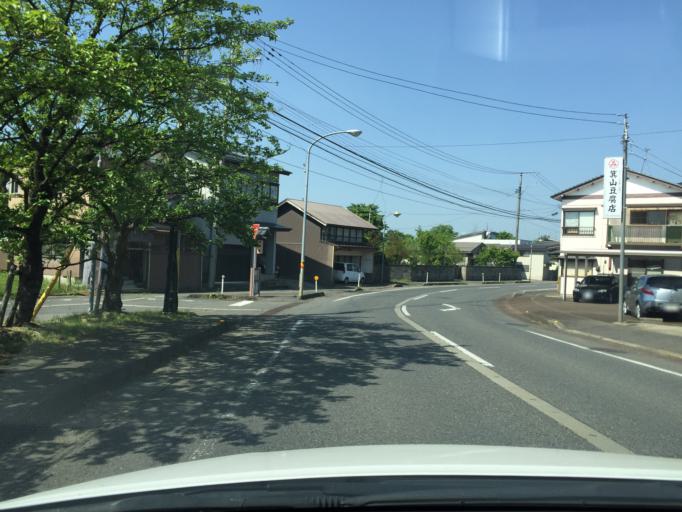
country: JP
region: Niigata
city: Muramatsu
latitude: 37.6886
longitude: 139.1716
